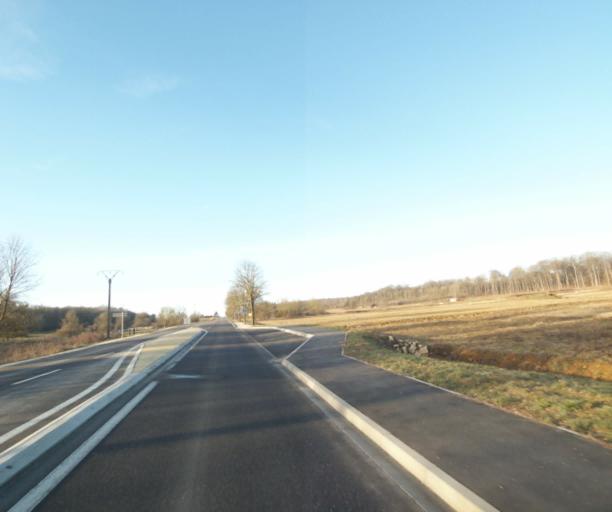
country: FR
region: Lorraine
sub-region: Departement de Meurthe-et-Moselle
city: Chavigny
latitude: 48.6429
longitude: 6.1352
